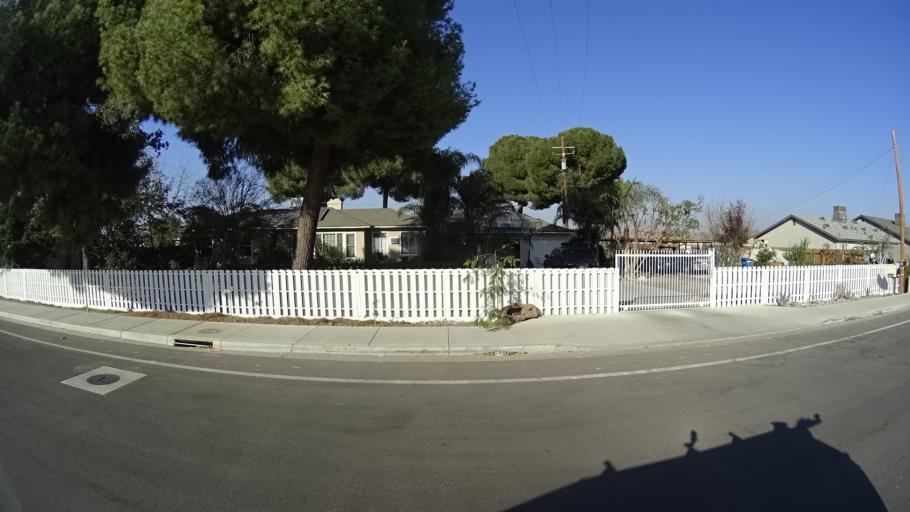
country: US
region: California
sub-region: Kern County
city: Greenfield
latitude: 35.2959
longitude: -118.9991
